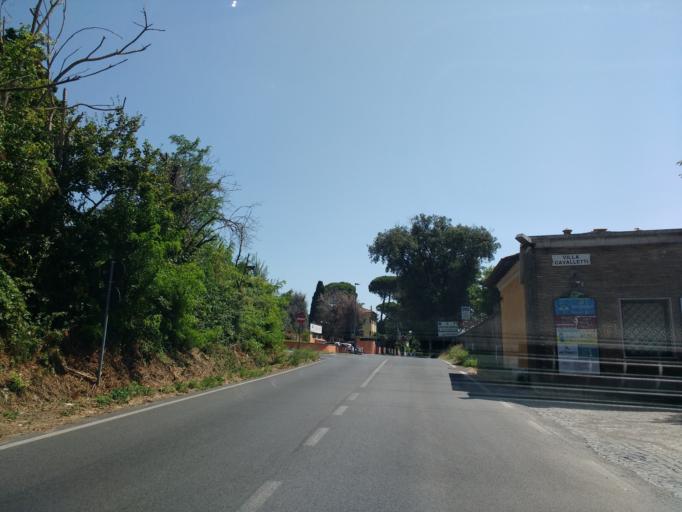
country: IT
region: Latium
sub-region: Citta metropolitana di Roma Capitale
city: Grottaferrata
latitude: 41.7945
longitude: 12.6828
